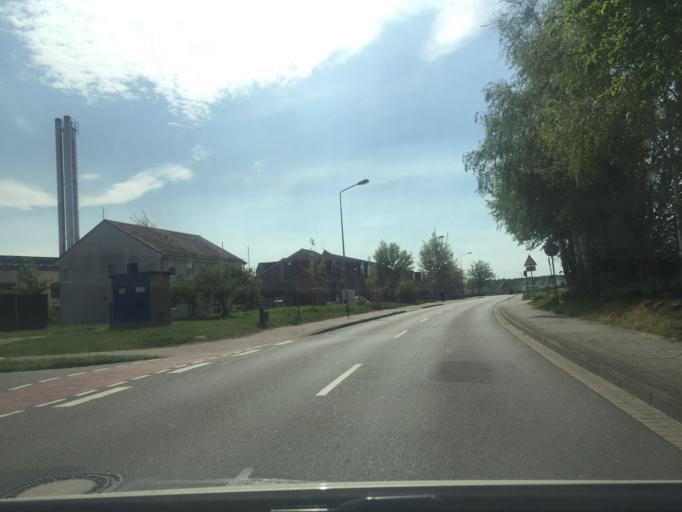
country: DE
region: Mecklenburg-Vorpommern
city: Torgelow
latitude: 53.6334
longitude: 14.0067
